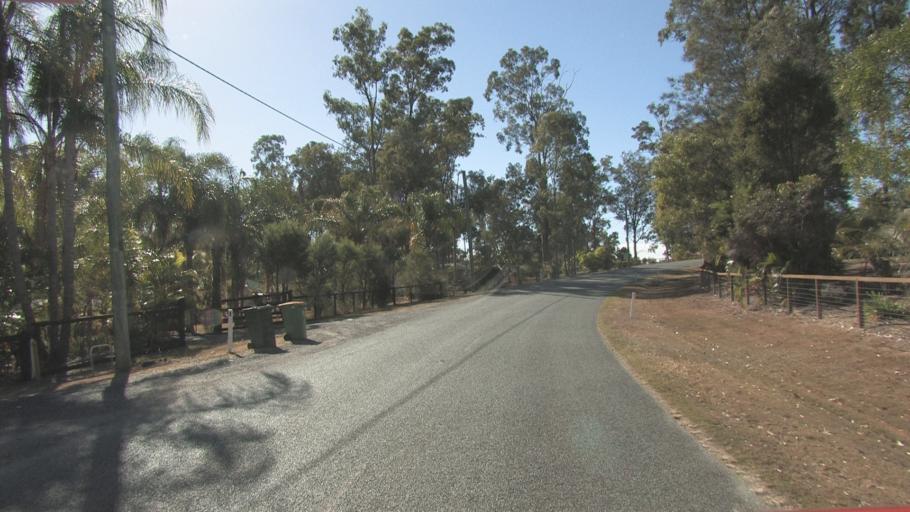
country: AU
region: Queensland
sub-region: Logan
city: Cedar Vale
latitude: -27.8826
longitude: 153.0013
